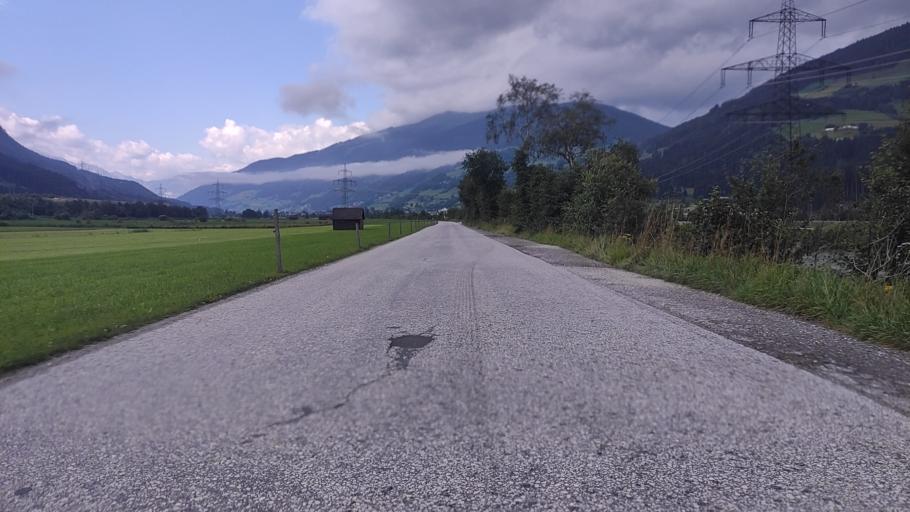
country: AT
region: Salzburg
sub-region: Politischer Bezirk Zell am See
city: Hollersbach im Pinzgau
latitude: 47.2787
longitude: 12.4067
